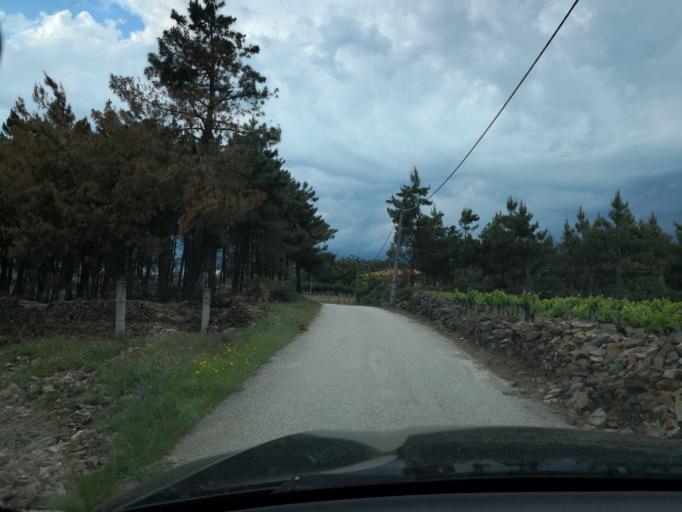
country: PT
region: Vila Real
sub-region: Sabrosa
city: Vilela
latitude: 41.2198
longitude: -7.6687
